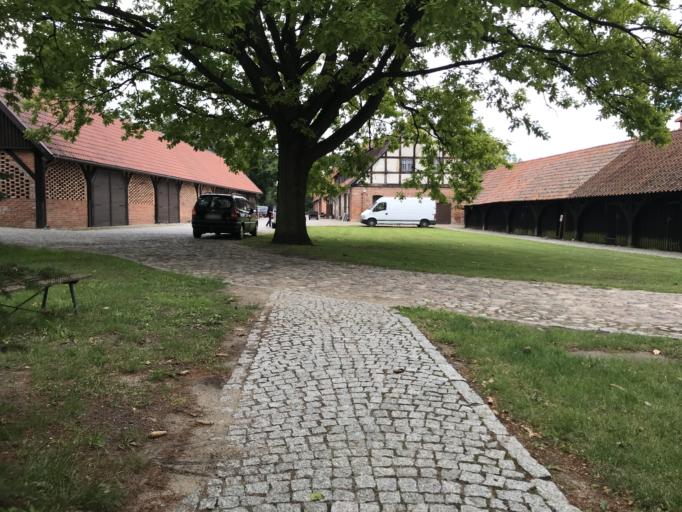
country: PL
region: Pomeranian Voivodeship
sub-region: Powiat malborski
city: Malbork
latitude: 54.0415
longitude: 19.0310
